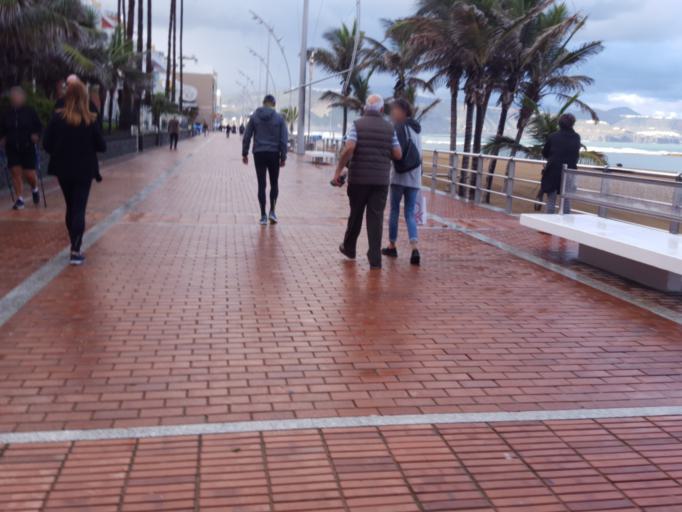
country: ES
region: Canary Islands
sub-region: Provincia de Las Palmas
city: Las Palmas de Gran Canaria
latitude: 28.1430
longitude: -15.4331
